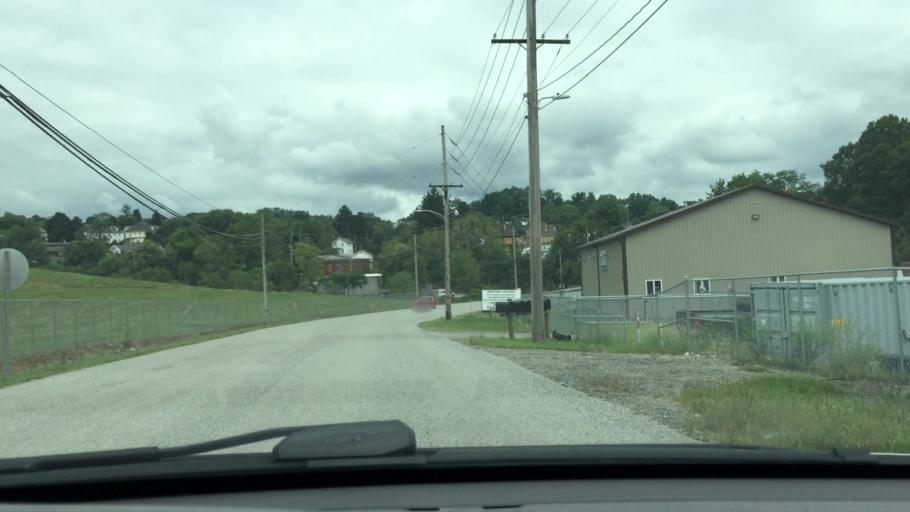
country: US
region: Pennsylvania
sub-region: Washington County
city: Canonsburg
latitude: 40.2552
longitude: -80.1979
